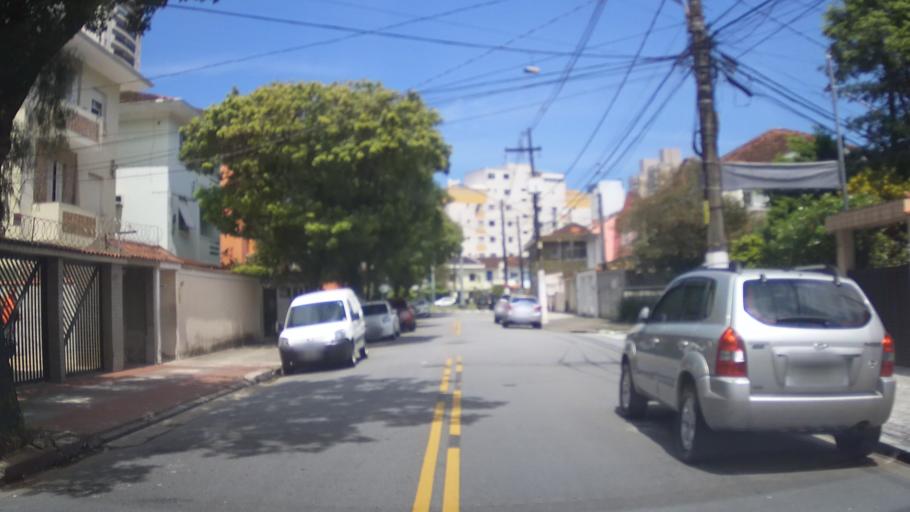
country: BR
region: Sao Paulo
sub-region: Santos
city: Santos
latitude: -23.9623
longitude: -46.3465
